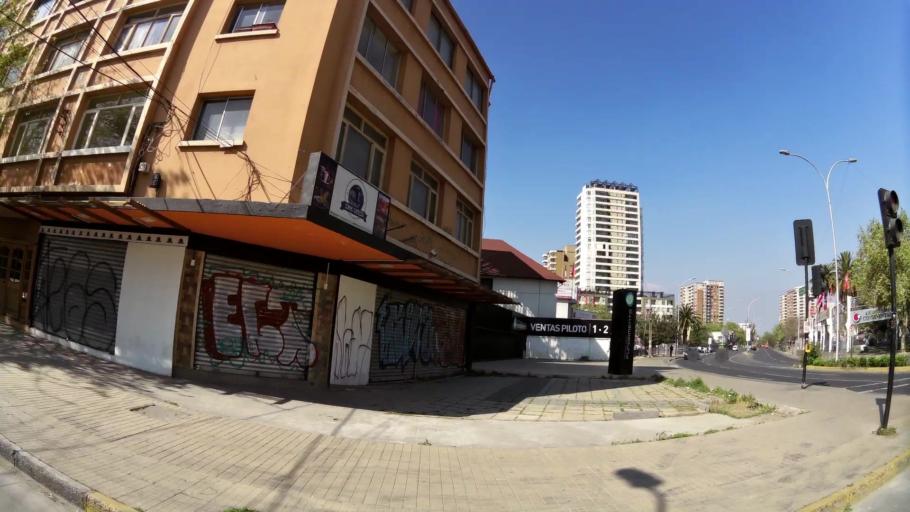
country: CL
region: Santiago Metropolitan
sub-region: Provincia de Santiago
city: Santiago
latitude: -33.4522
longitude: -70.6258
